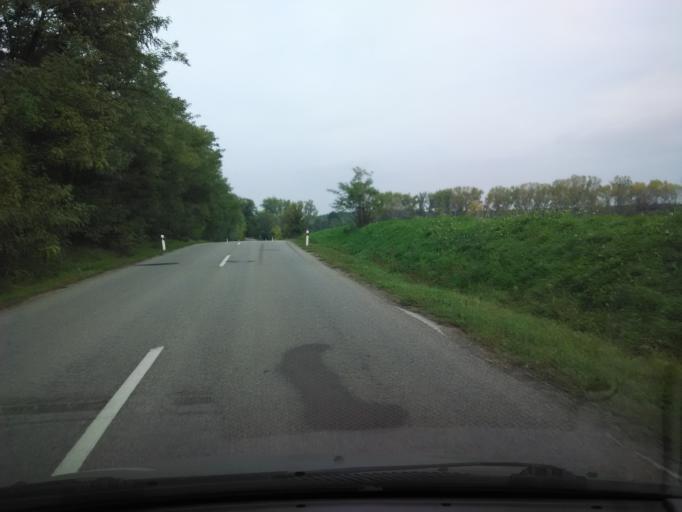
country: SK
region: Nitriansky
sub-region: Okres Nove Zamky
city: Nove Zamky
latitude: 47.9546
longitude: 18.2486
